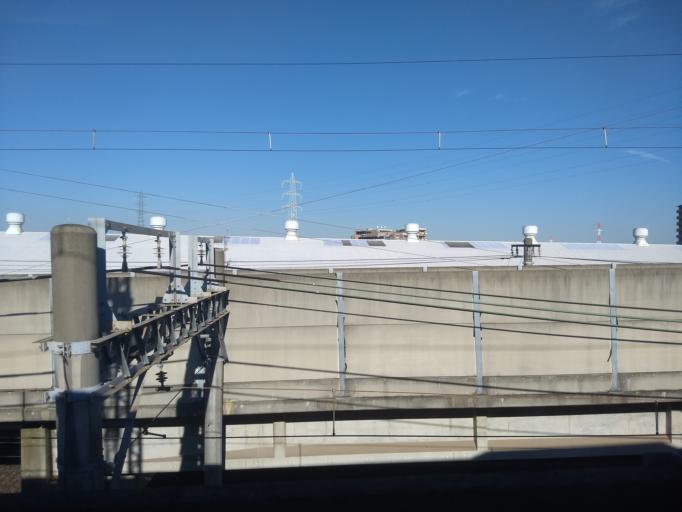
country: JP
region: Chiba
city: Matsudo
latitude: 35.7501
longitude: 139.8722
